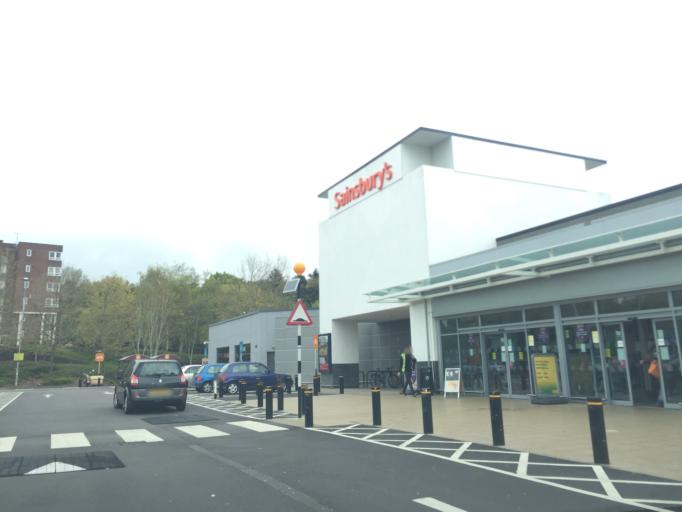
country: GB
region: England
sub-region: Essex
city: Harlow
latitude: 51.7738
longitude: 0.0936
